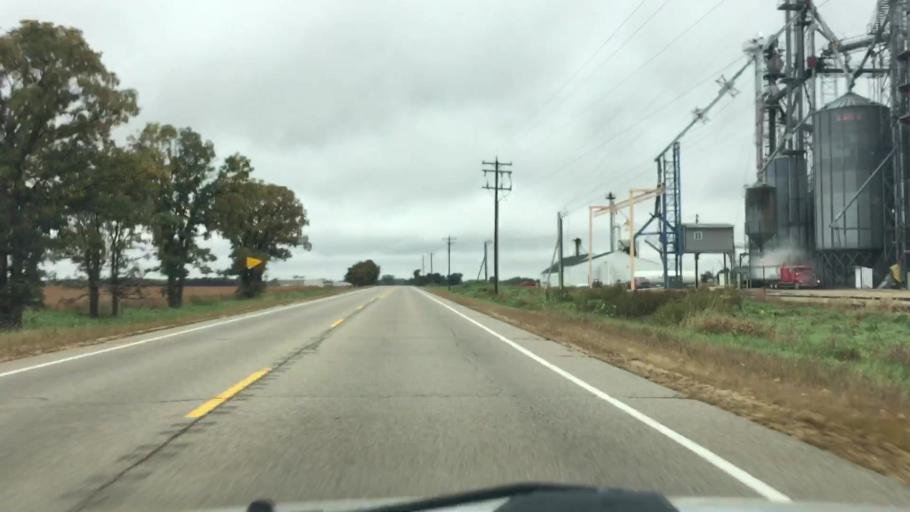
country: US
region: Wisconsin
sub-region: Walworth County
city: Whitewater
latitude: 42.8032
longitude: -88.7911
